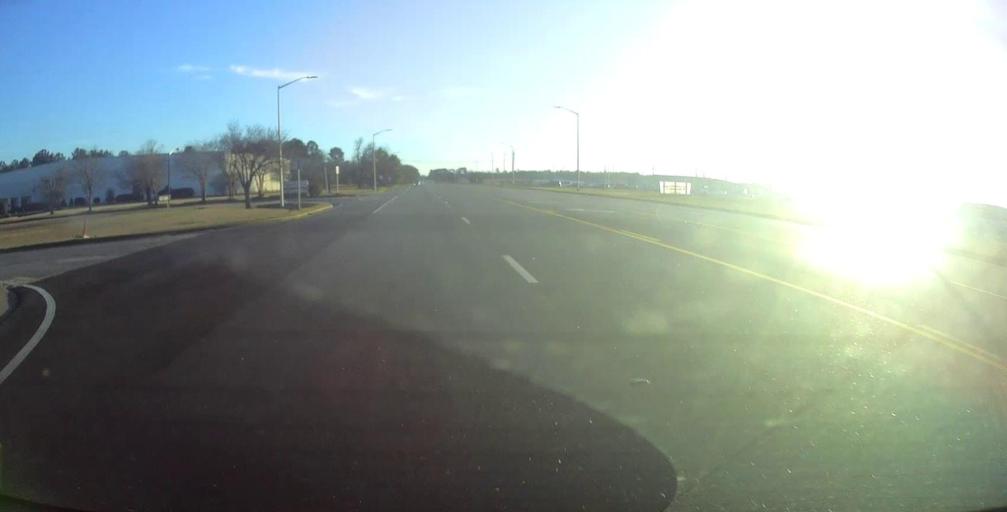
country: US
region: Georgia
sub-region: Dougherty County
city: Albany
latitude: 31.5322
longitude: -84.1871
